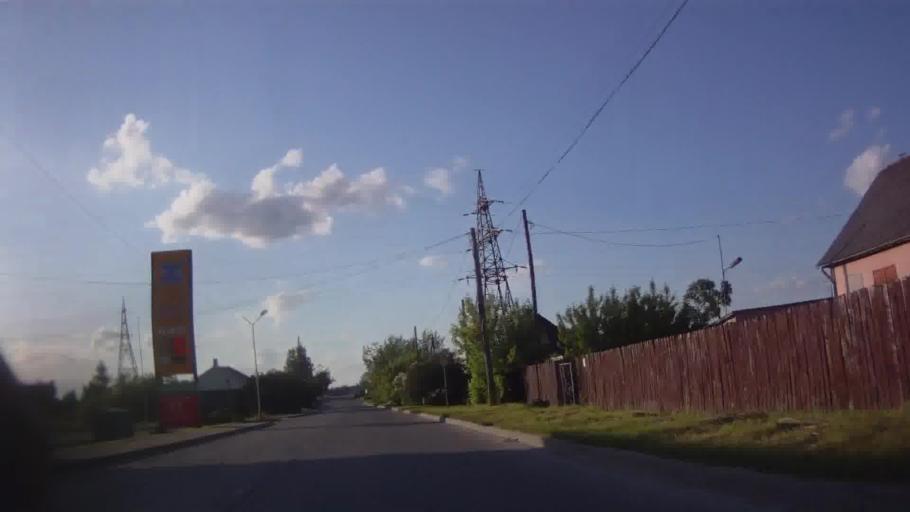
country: LV
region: Rezekne
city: Rezekne
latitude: 56.5191
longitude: 27.3209
